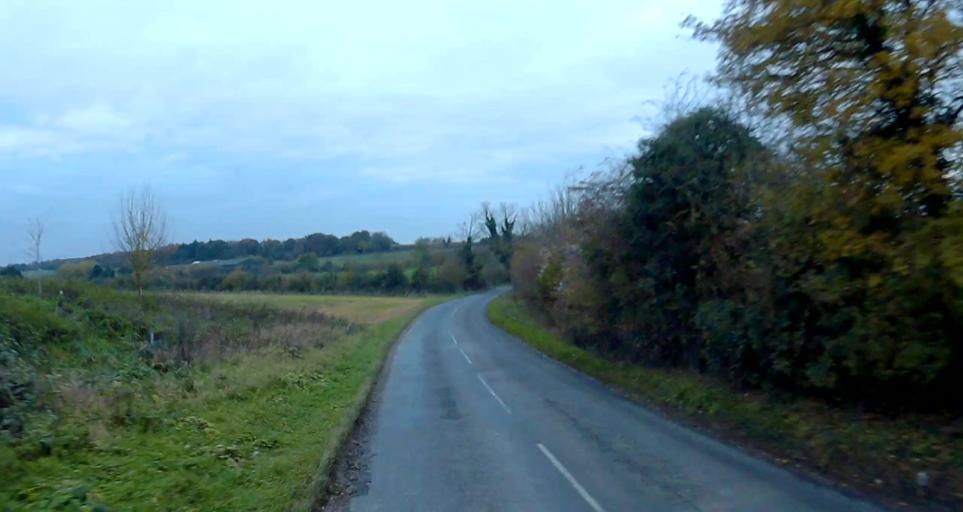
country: GB
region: England
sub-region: Hampshire
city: Odiham
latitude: 51.2449
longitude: -0.9731
